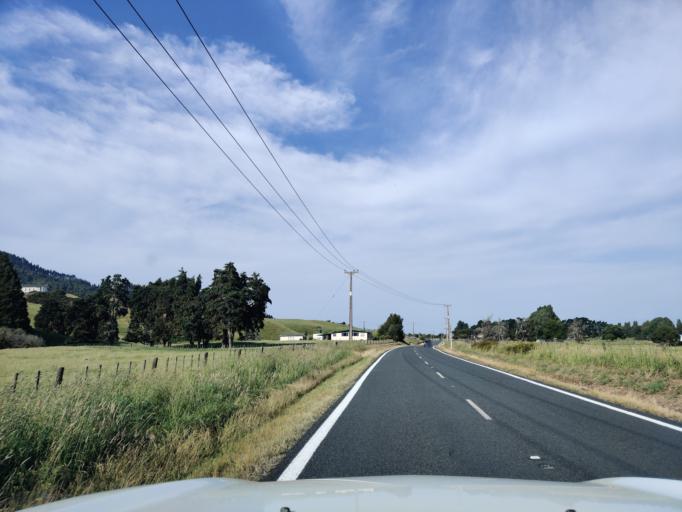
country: NZ
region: Waikato
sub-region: Waikato District
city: Ngaruawahia
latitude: -37.6291
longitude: 175.1645
